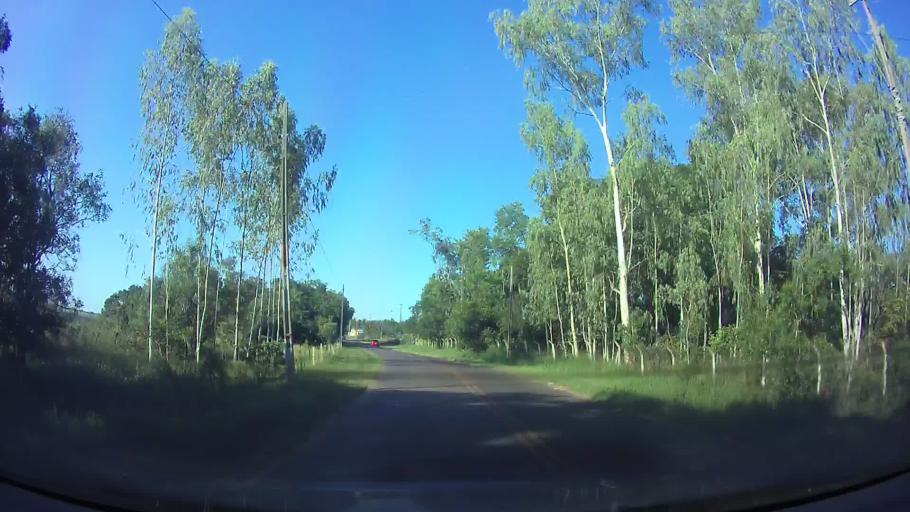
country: PY
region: Cordillera
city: Atyra
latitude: -25.3019
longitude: -57.1857
